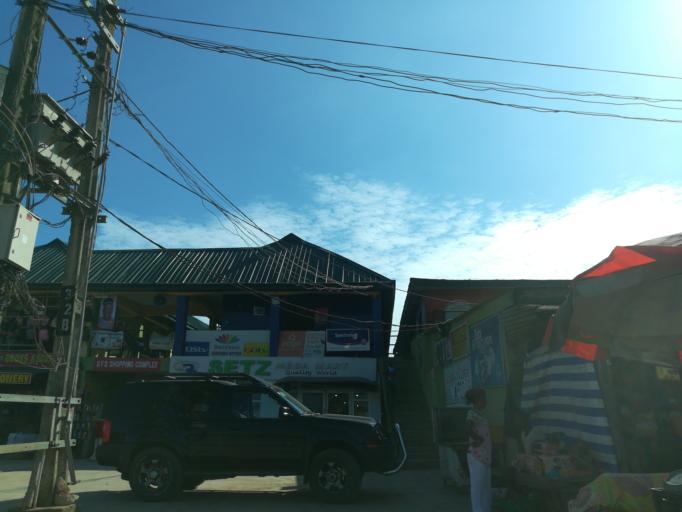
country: NG
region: Lagos
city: Ikorodu
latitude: 6.5876
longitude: 3.5199
